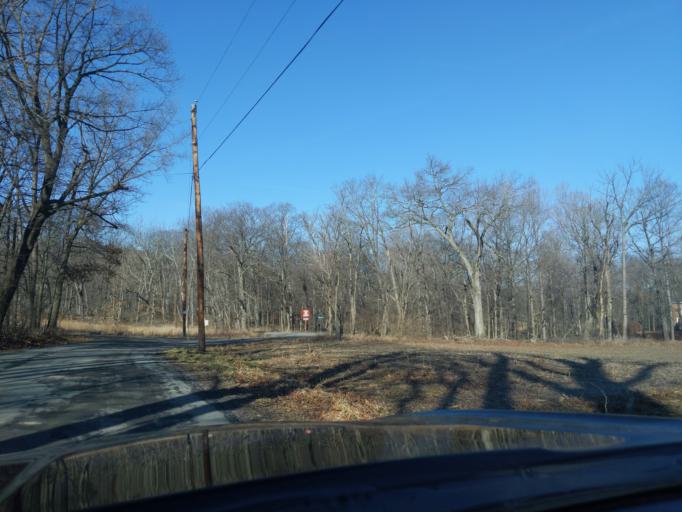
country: US
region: Pennsylvania
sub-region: Blair County
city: Bellwood
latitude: 40.5779
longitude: -78.2730
